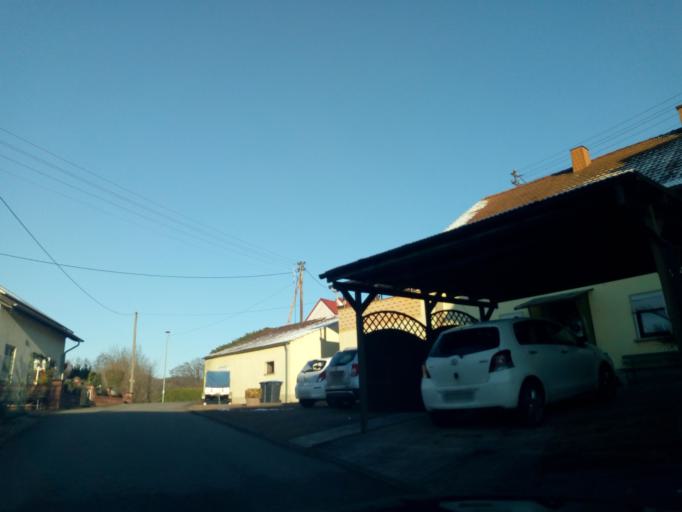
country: DE
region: Saarland
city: Heusweiler
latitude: 49.3602
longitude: 6.9369
